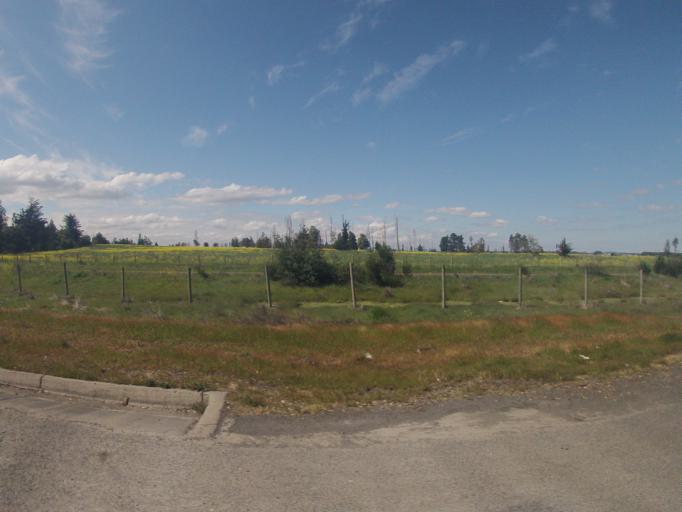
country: CL
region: Biobio
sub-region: Provincia de Biobio
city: Los Angeles
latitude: -37.4483
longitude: -72.4059
